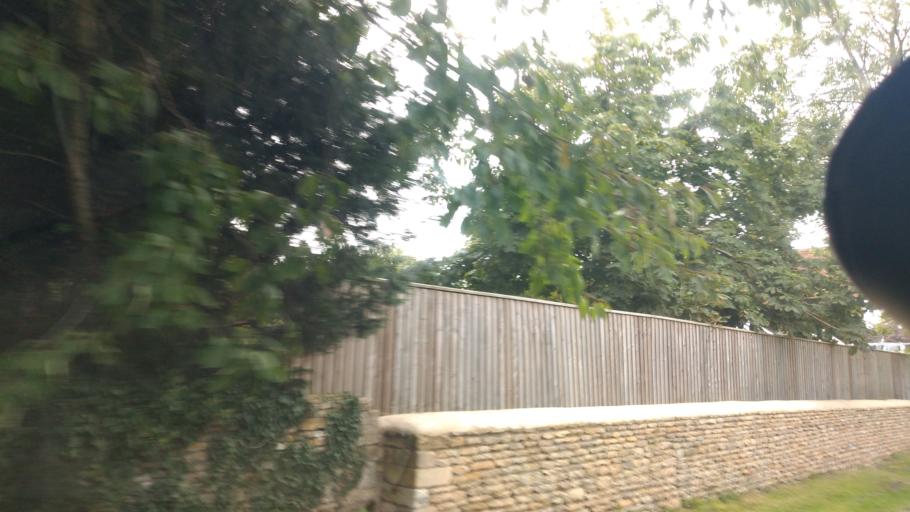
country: GB
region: England
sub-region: Wiltshire
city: Corsham
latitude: 51.4341
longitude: -2.1651
